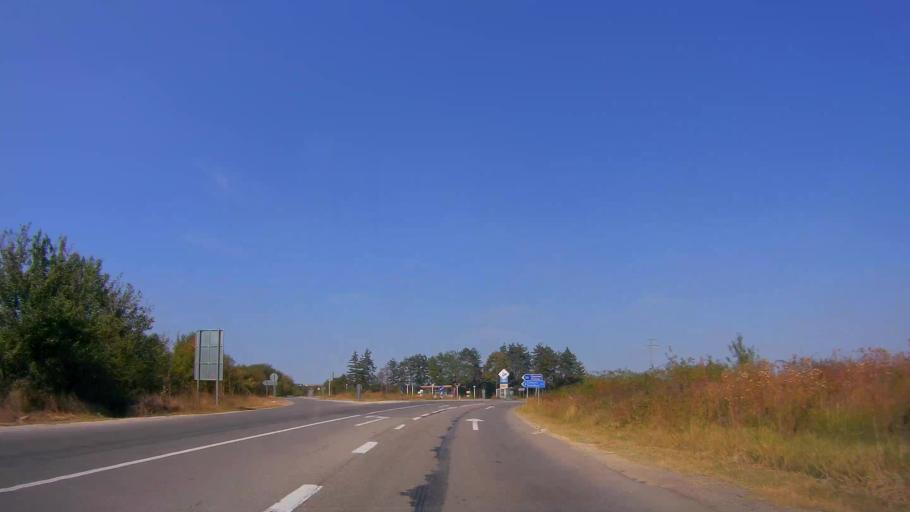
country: BG
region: Shumen
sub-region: Obshtina Smyadovo
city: Smyadovo
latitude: 43.0561
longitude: 27.0412
